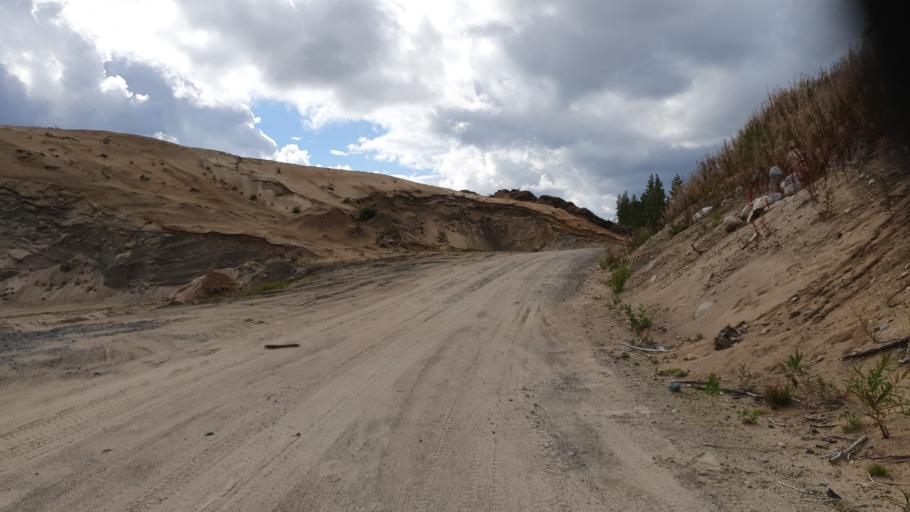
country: FI
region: Kainuu
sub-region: Kehys-Kainuu
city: Kuhmo
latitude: 64.1516
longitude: 29.3714
